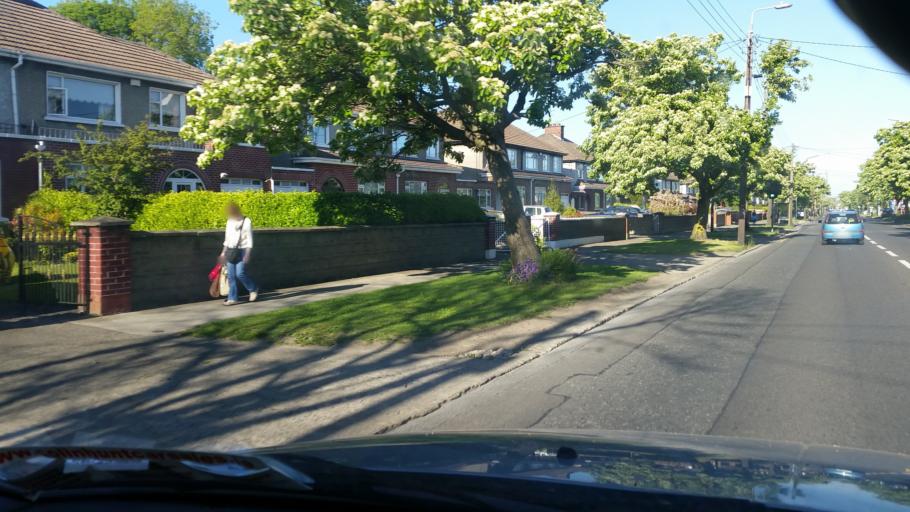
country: IE
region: Leinster
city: Ballymun
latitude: 53.3902
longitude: -6.2755
